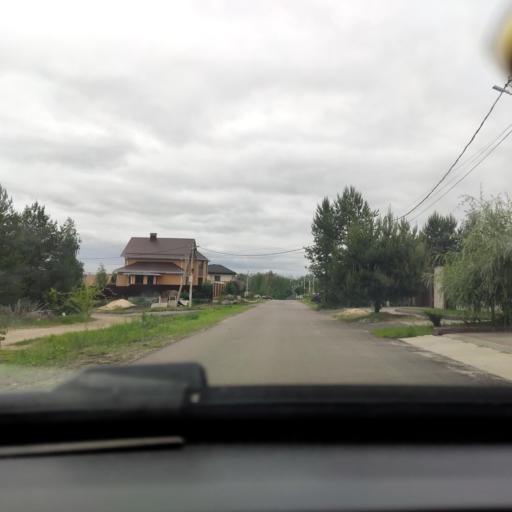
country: RU
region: Voronezj
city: Podgornoye
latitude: 51.8136
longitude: 39.1346
